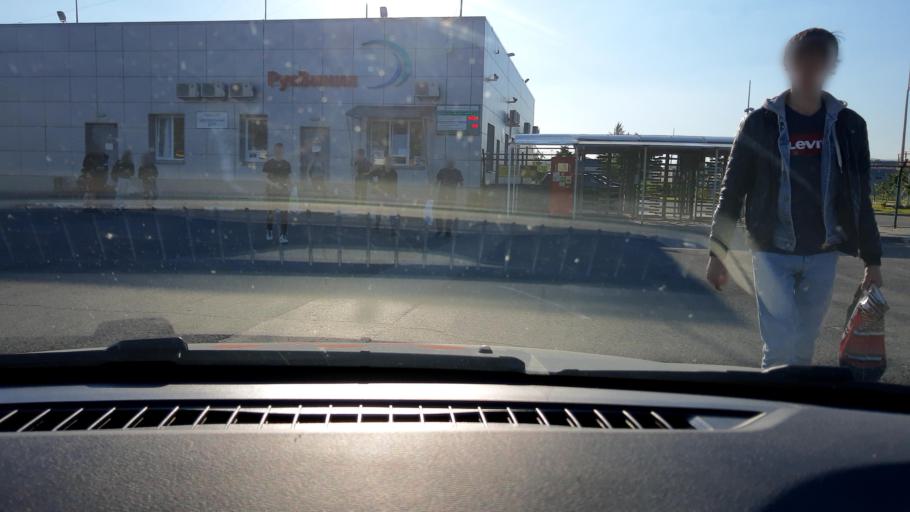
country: RU
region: Nizjnij Novgorod
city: Kstovo
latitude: 56.1071
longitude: 44.1262
